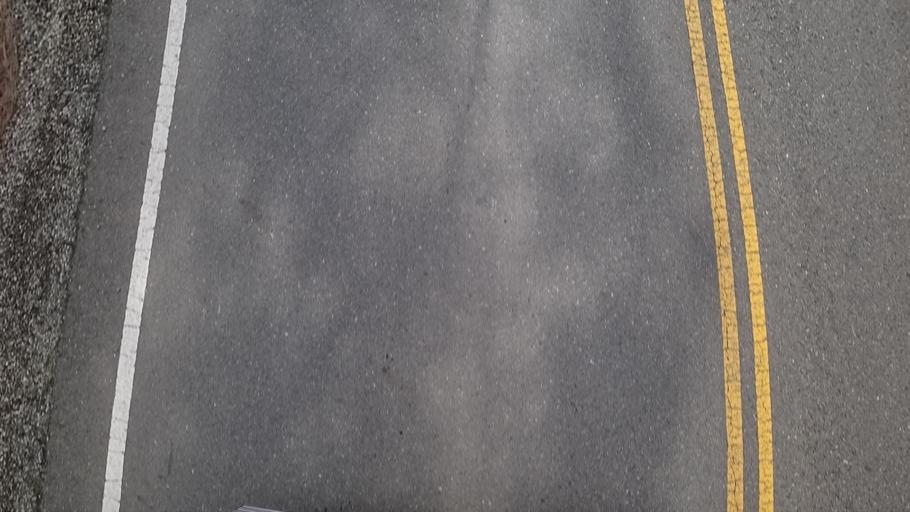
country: US
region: California
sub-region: Yuba County
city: Loma Rica
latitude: 39.4133
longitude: -121.4227
